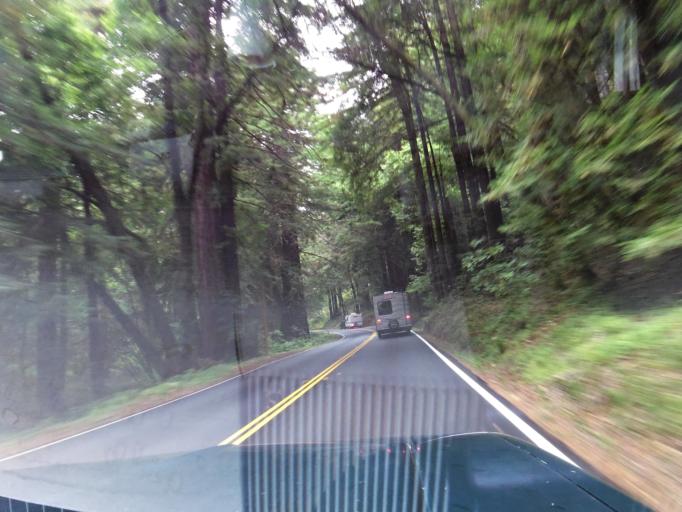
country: US
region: California
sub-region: Mendocino County
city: Fort Bragg
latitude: 39.1832
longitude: -123.7143
